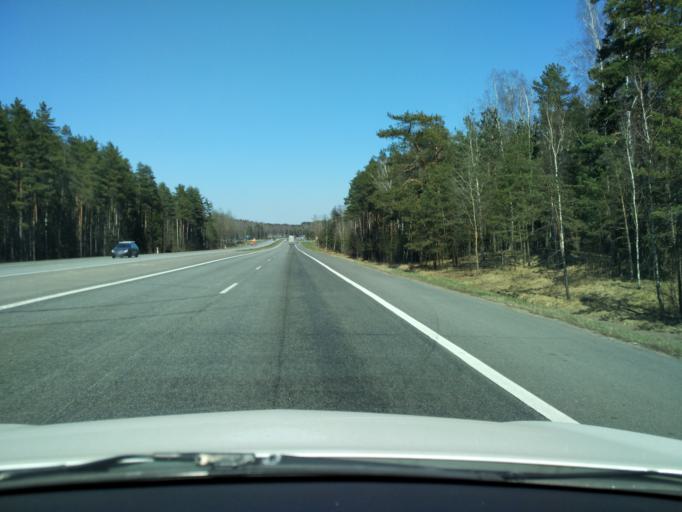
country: BY
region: Minsk
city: Slabada
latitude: 53.9279
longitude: 27.9587
